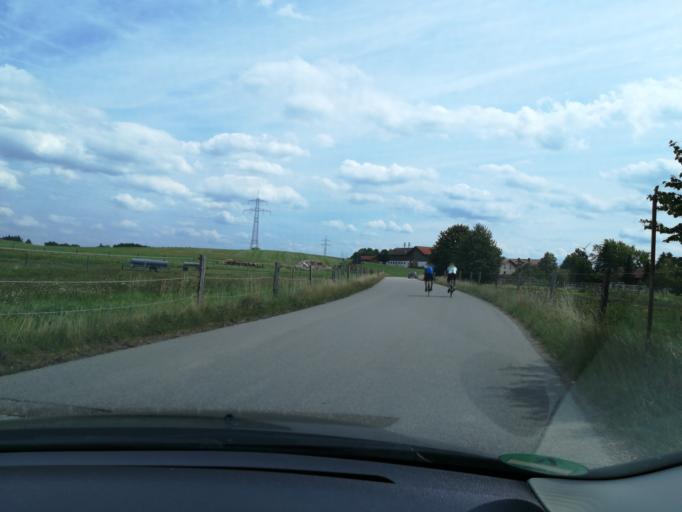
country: DE
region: Bavaria
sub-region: Upper Bavaria
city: Bruck
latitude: 48.0254
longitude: 11.9275
